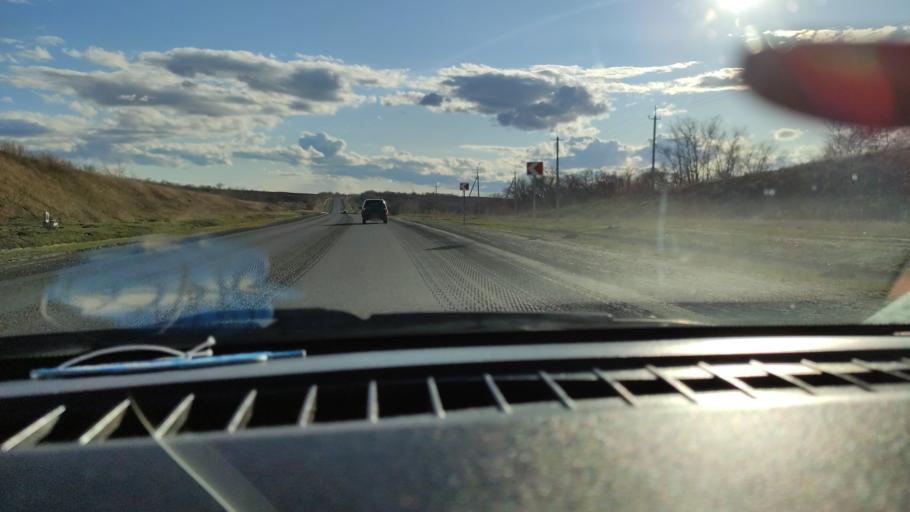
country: RU
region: Saratov
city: Shumeyka
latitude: 51.7781
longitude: 46.1177
